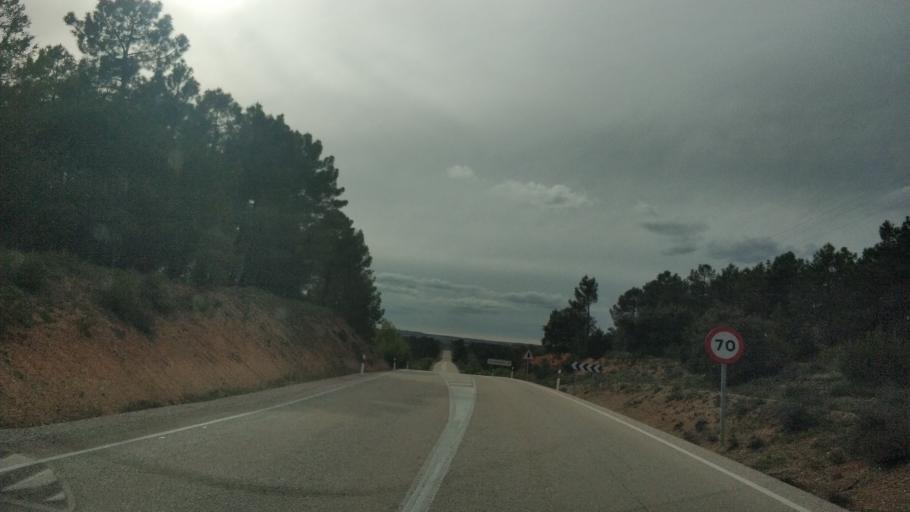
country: ES
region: Castille and Leon
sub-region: Provincia de Soria
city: Valdenebro
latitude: 41.5586
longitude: -2.9699
